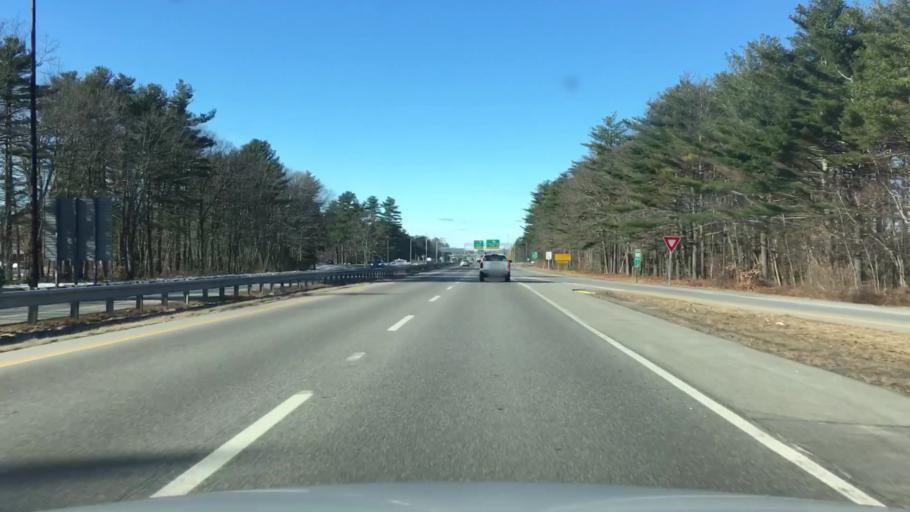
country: US
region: Maine
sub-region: Cumberland County
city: South Portland Gardens
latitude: 43.6277
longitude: -70.3309
